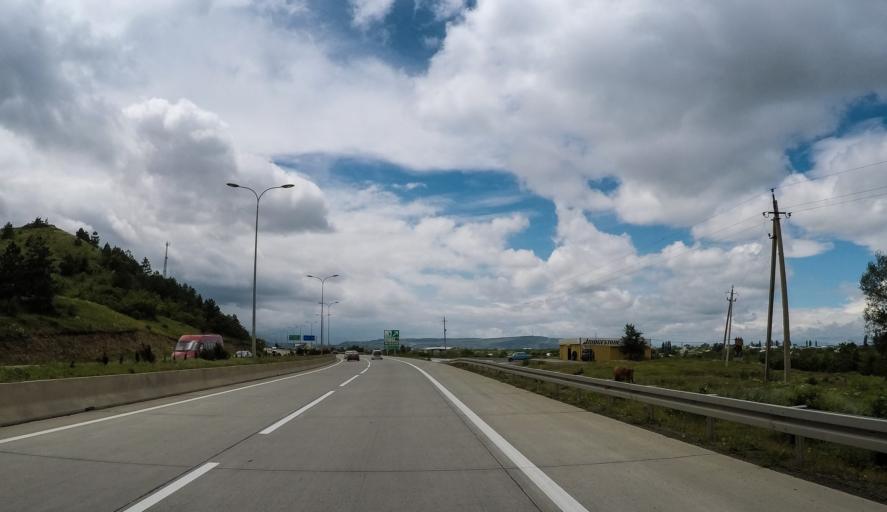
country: GE
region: Shida Kartli
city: Gori
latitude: 42.0202
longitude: 44.1534
